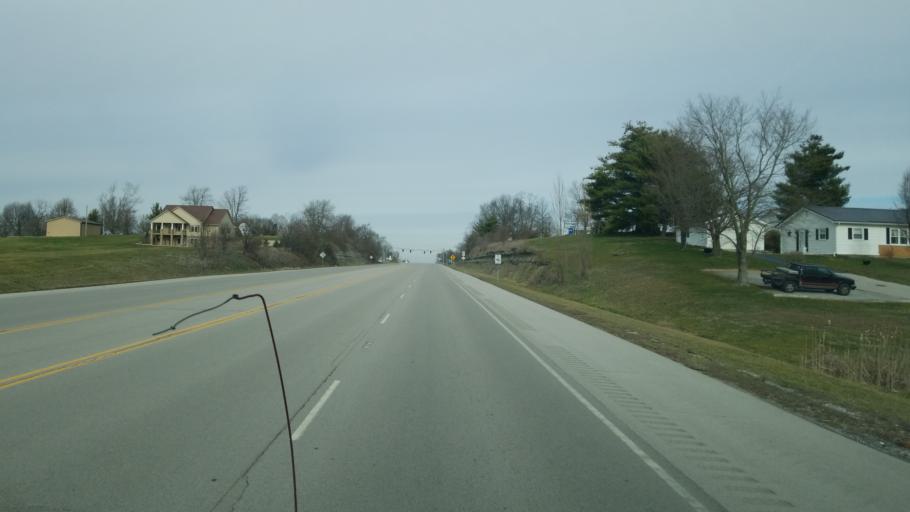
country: US
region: Ohio
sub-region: Brown County
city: Aberdeen
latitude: 38.6082
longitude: -83.8110
